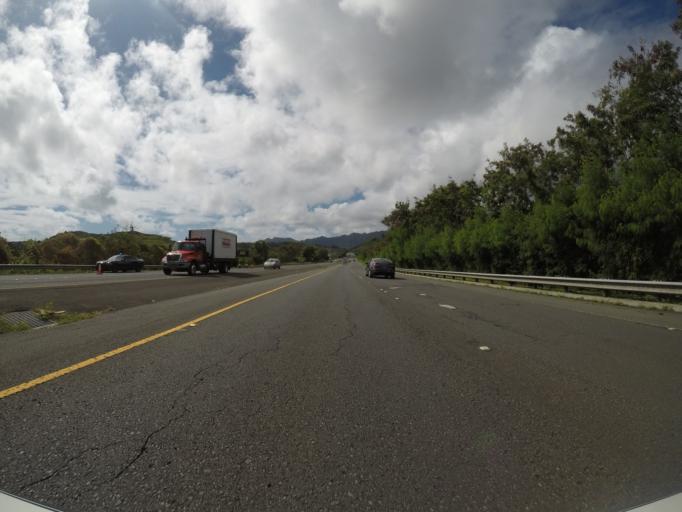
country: US
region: Hawaii
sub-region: Honolulu County
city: Maunawili
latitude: 21.3704
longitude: -157.7419
